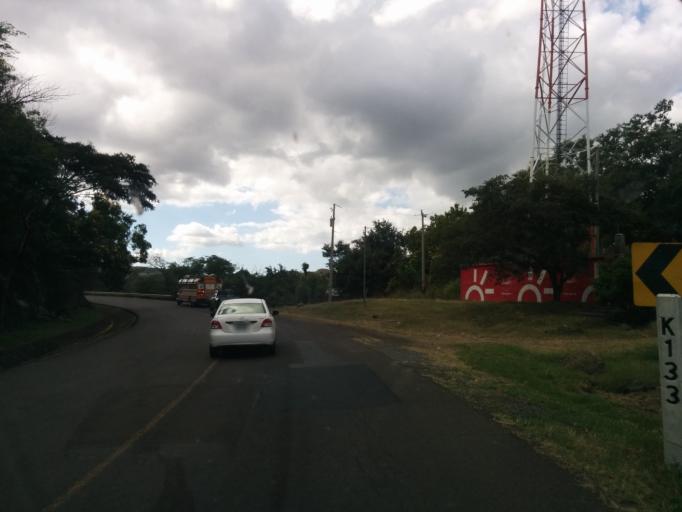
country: NI
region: Esteli
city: Esteli
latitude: 12.9991
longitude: -86.2849
